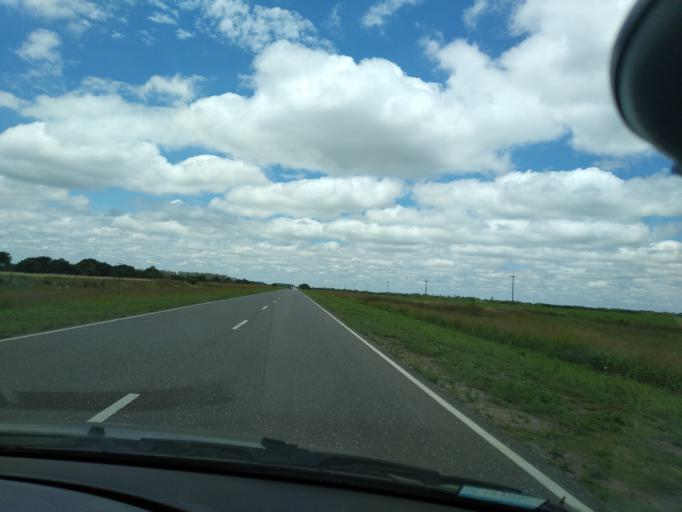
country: AR
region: Cordoba
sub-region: Departamento de Rio Segundo
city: Rio Segundo
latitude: -31.6435
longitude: -63.9681
